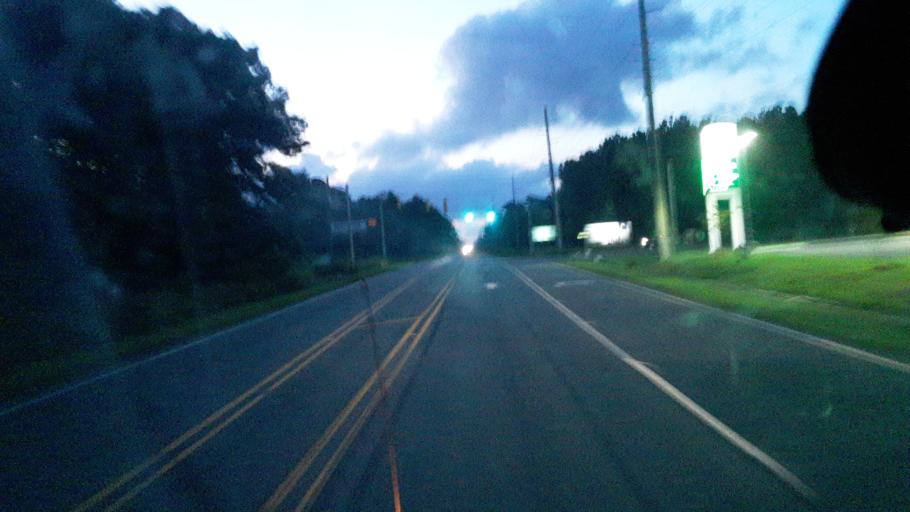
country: US
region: North Carolina
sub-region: Brunswick County
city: Oak Island
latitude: 33.9862
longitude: -78.1898
